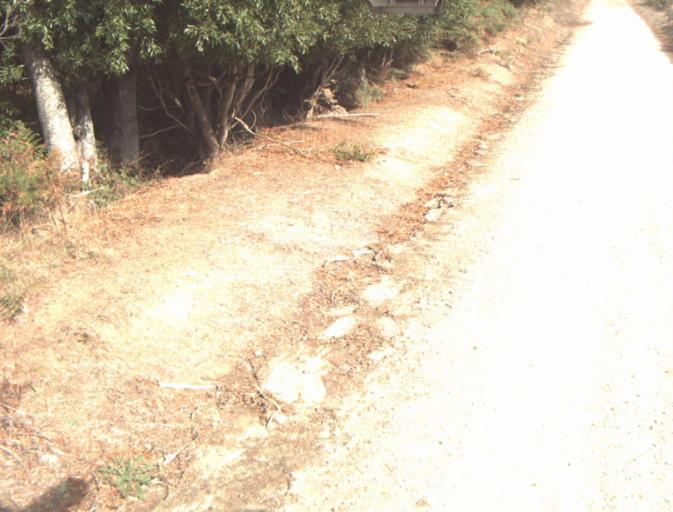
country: AU
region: Tasmania
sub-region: Launceston
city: Mayfield
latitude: -41.1810
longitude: 147.1944
